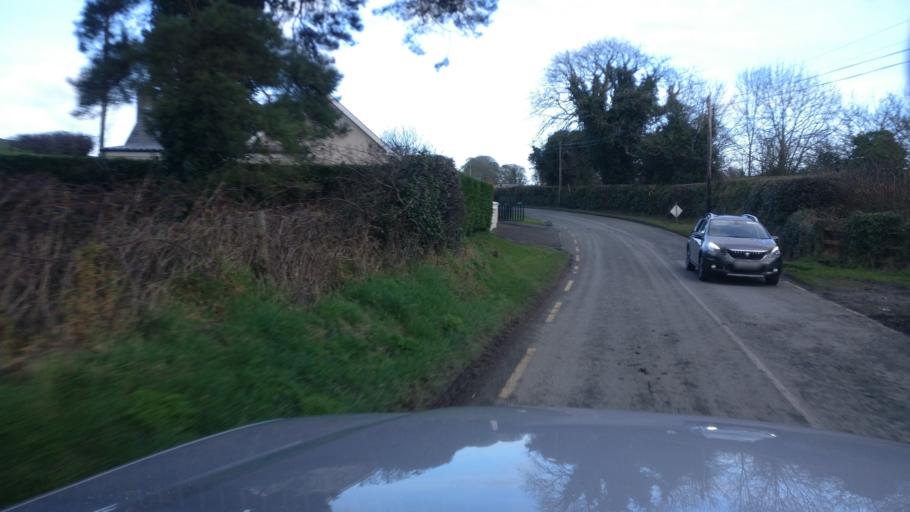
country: IE
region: Leinster
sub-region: Kilkenny
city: Castlecomer
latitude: 52.8218
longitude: -7.2117
